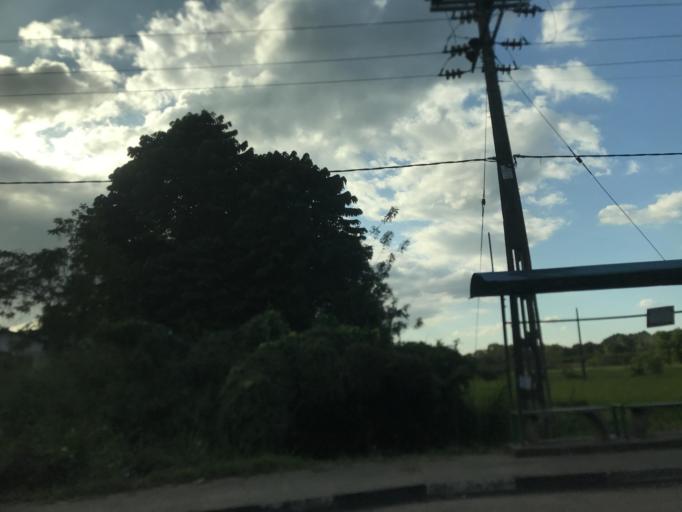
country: LK
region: Western
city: Gampaha
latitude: 7.0933
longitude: 79.9903
